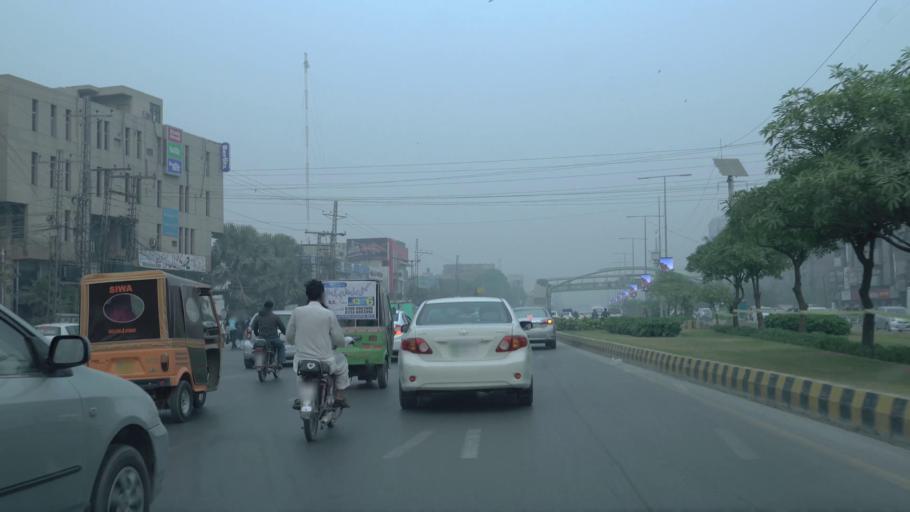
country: PK
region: Punjab
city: Lahore
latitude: 31.4999
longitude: 74.3174
